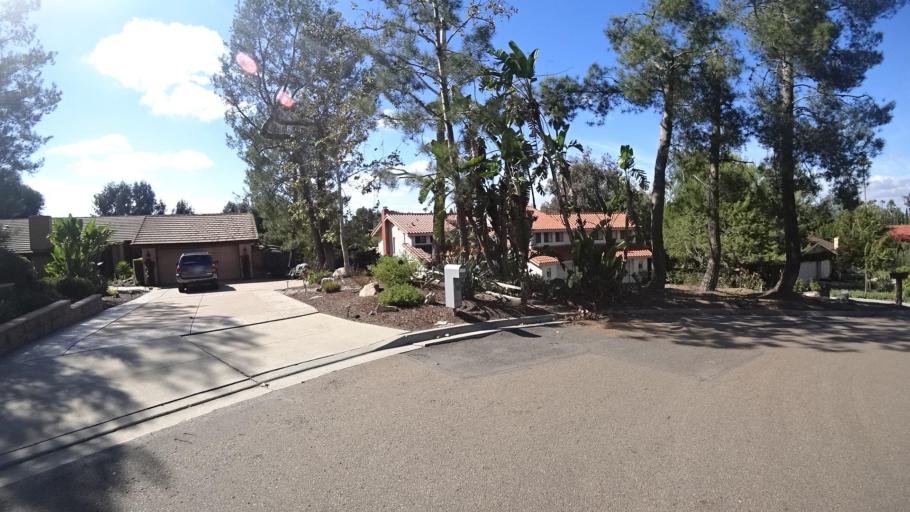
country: US
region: California
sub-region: San Diego County
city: Rancho San Diego
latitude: 32.7681
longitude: -116.9356
